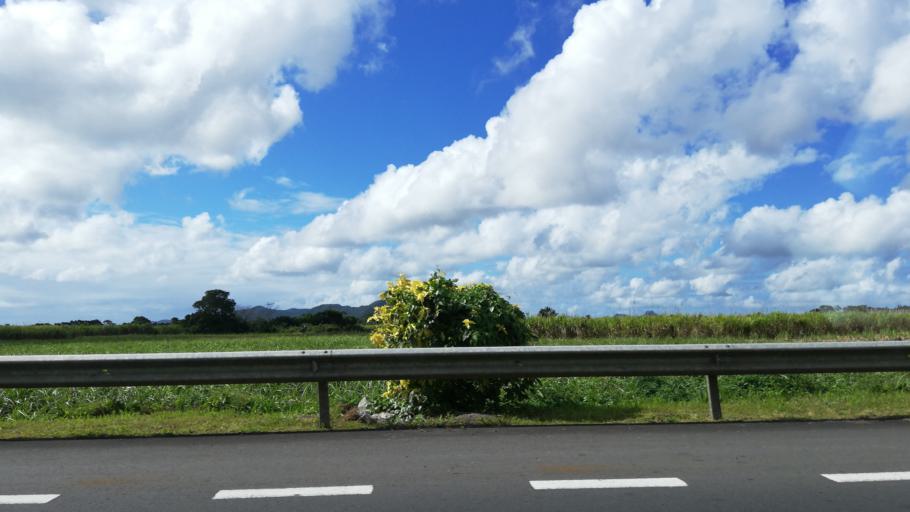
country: MU
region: Flacq
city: Saint Julien
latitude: -20.2374
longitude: 57.6269
